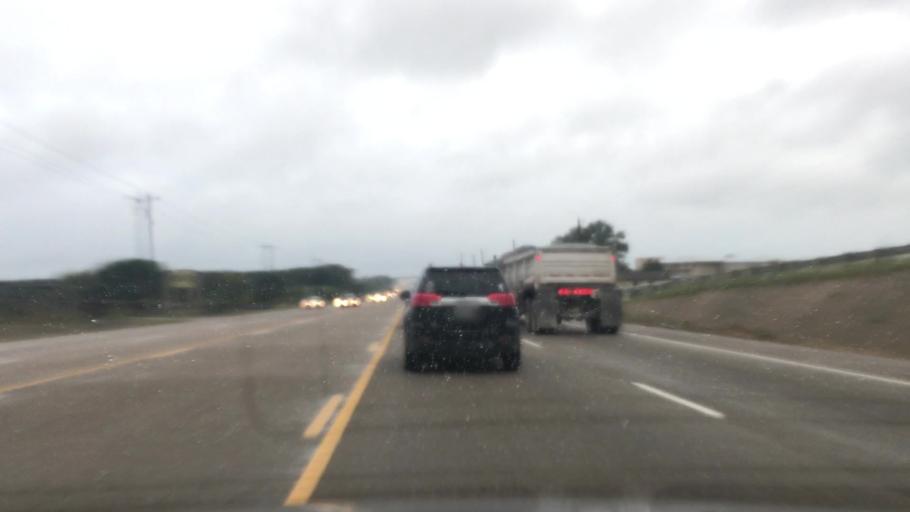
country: US
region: Texas
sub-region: Denton County
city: Cross Roads
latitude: 33.2273
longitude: -96.9926
